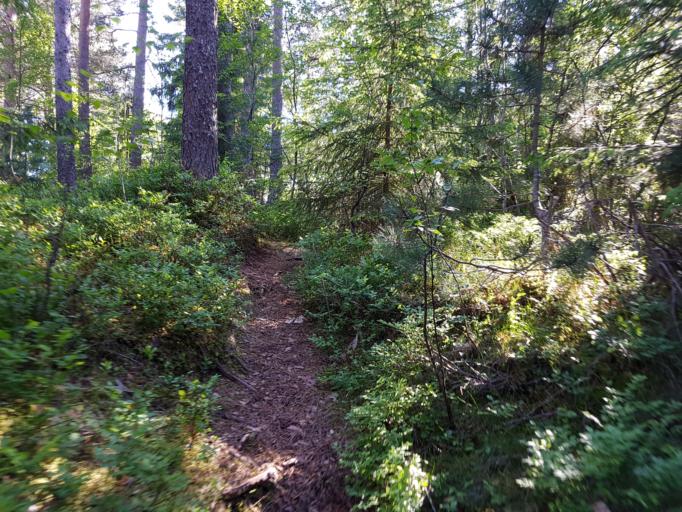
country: NO
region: Sor-Trondelag
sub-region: Trondheim
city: Trondheim
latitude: 63.4217
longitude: 10.3634
